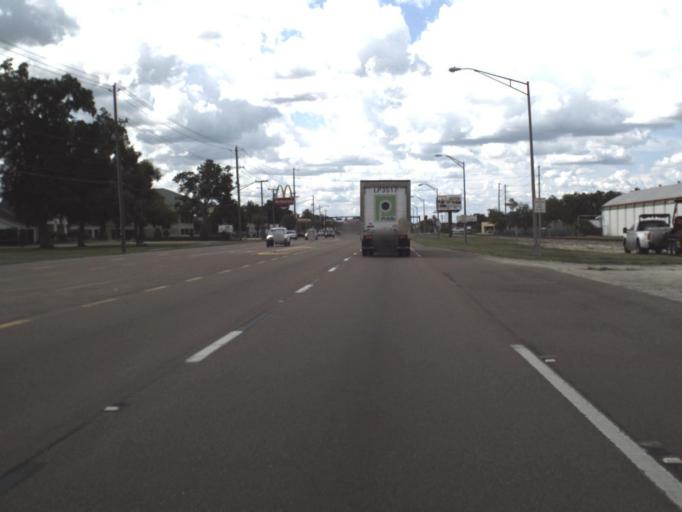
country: US
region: Florida
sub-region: Polk County
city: Crystal Lake
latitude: 28.0215
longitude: -81.9220
